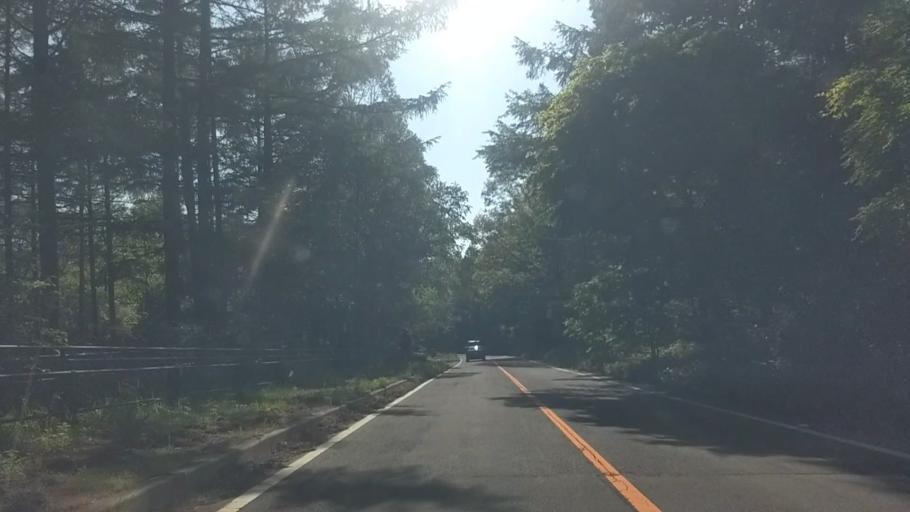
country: JP
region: Nagano
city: Chino
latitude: 35.8990
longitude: 138.3375
